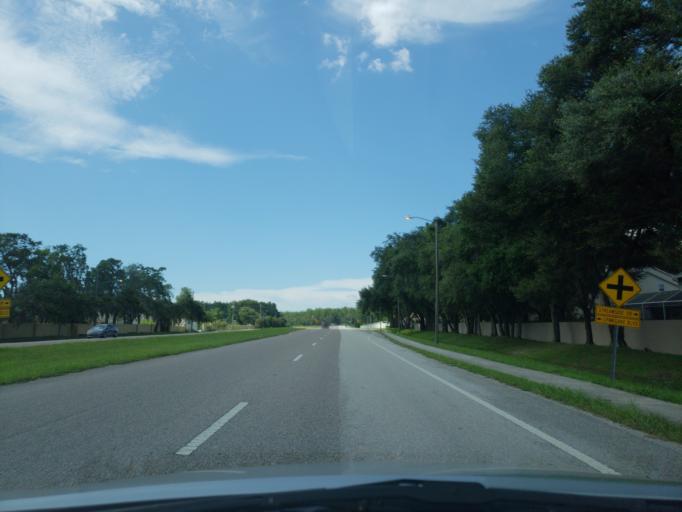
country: US
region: Florida
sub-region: Hillsborough County
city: Carrollwood Village
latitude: 28.0463
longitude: -82.5419
